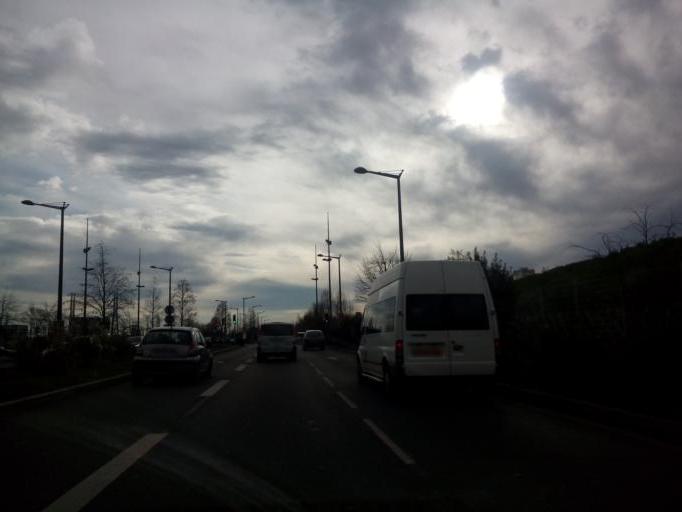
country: FR
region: Rhone-Alpes
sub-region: Departement du Rhone
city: Saint-Fons
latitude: 45.7235
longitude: 4.8422
